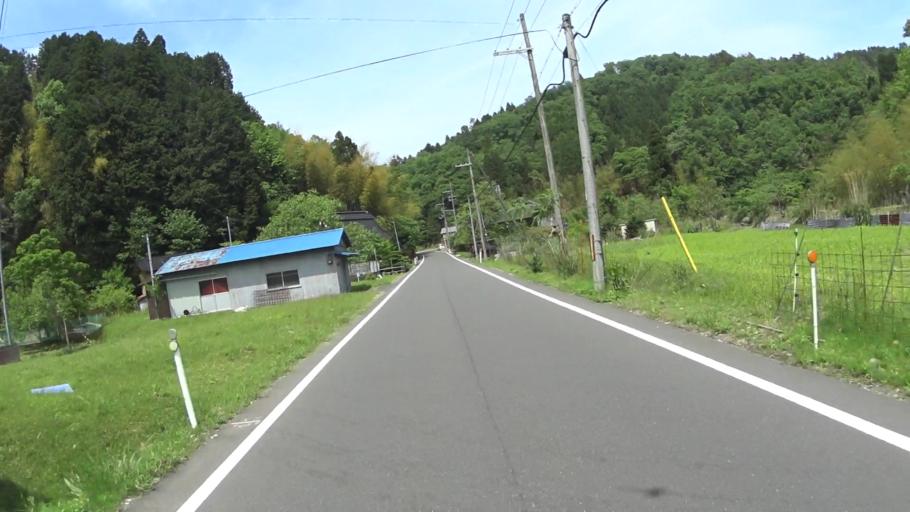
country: JP
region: Kyoto
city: Maizuru
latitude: 35.4303
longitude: 135.4781
